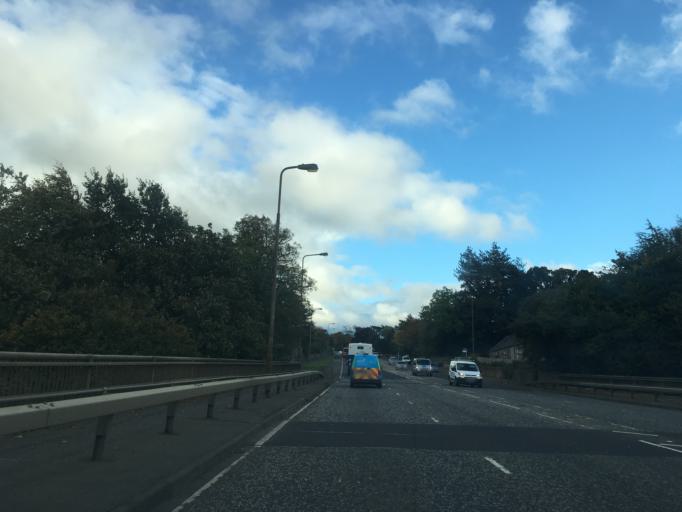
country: GB
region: Scotland
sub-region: Edinburgh
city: Currie
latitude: 55.9642
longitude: -3.3163
